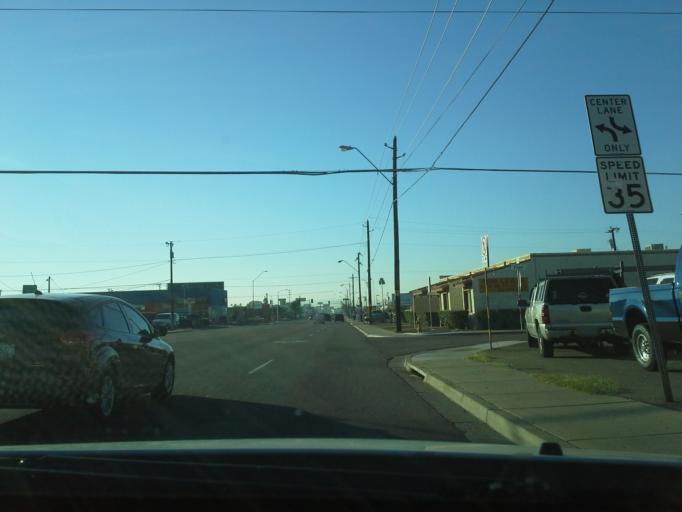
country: US
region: Arizona
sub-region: Maricopa County
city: Phoenix
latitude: 33.5735
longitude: -112.0653
